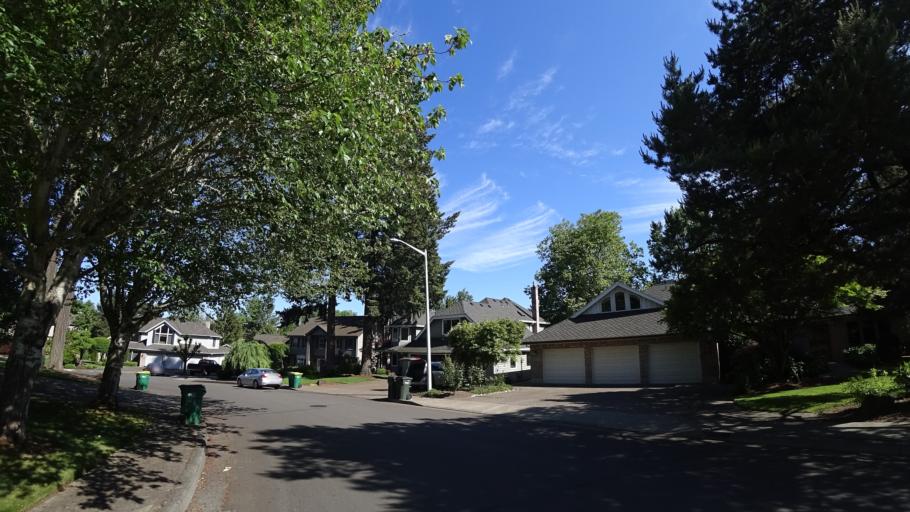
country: US
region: Oregon
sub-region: Washington County
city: Beaverton
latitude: 45.4453
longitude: -122.8170
